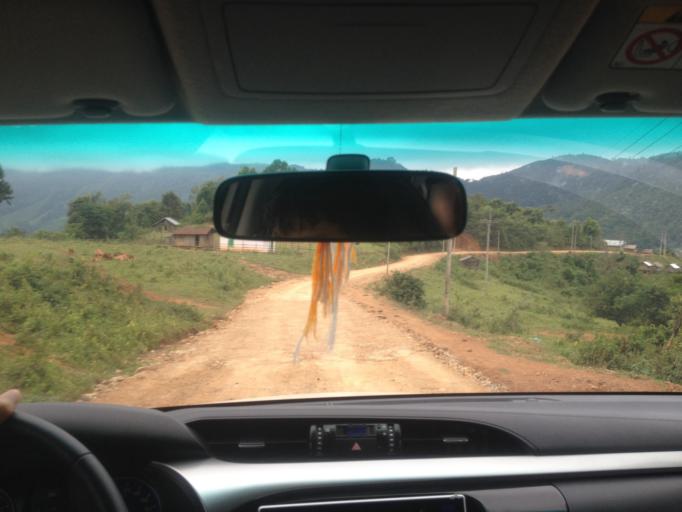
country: TH
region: Nan
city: Chaloem Phra Kiat
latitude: 19.9968
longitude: 101.1308
